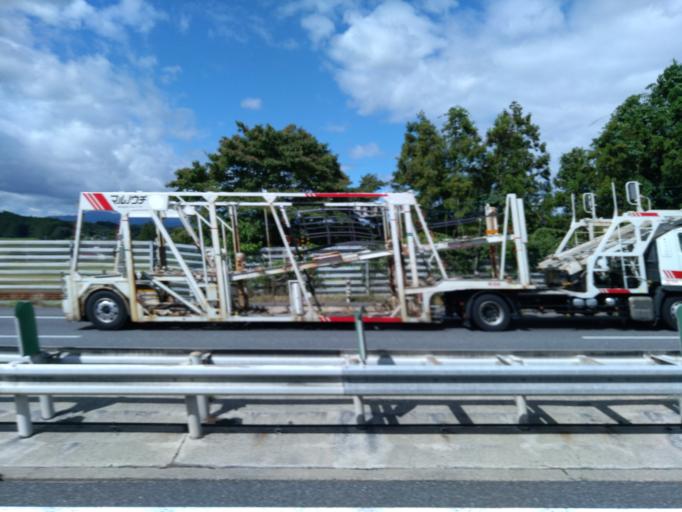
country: JP
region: Miyagi
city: Furukawa
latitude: 38.4849
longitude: 140.9251
